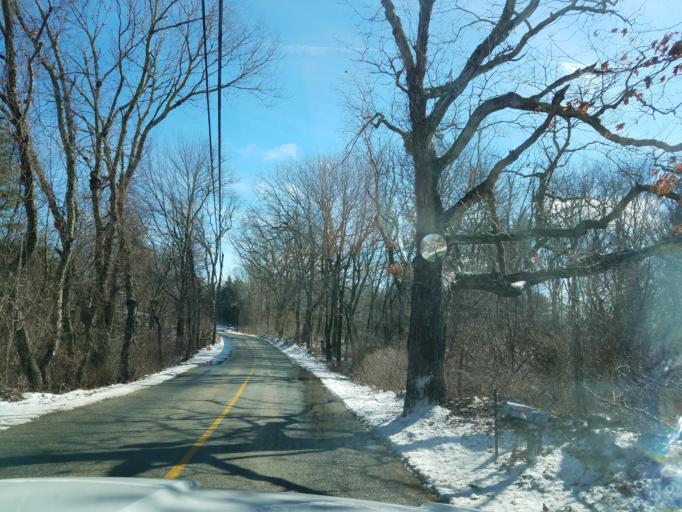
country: US
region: Connecticut
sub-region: New London County
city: Preston City
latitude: 41.4968
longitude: -71.9026
